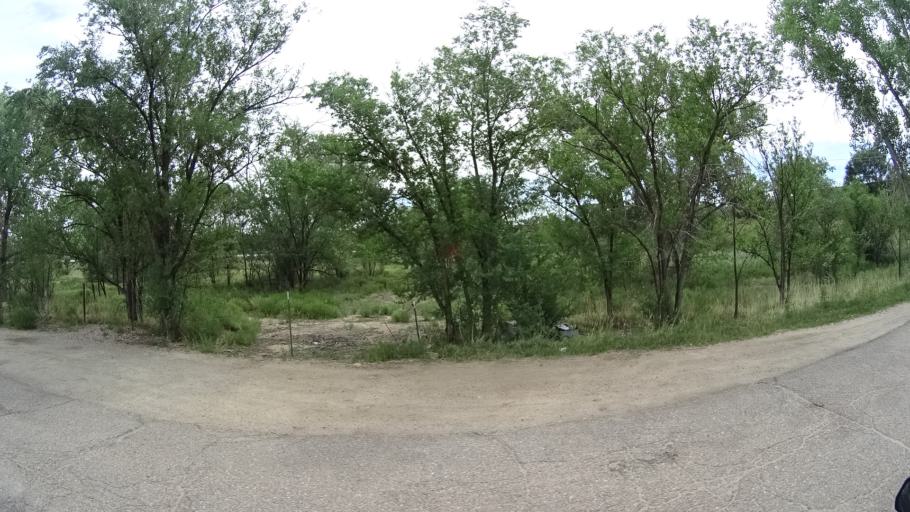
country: US
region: Colorado
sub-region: El Paso County
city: Fountain
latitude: 38.6789
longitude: -104.7151
